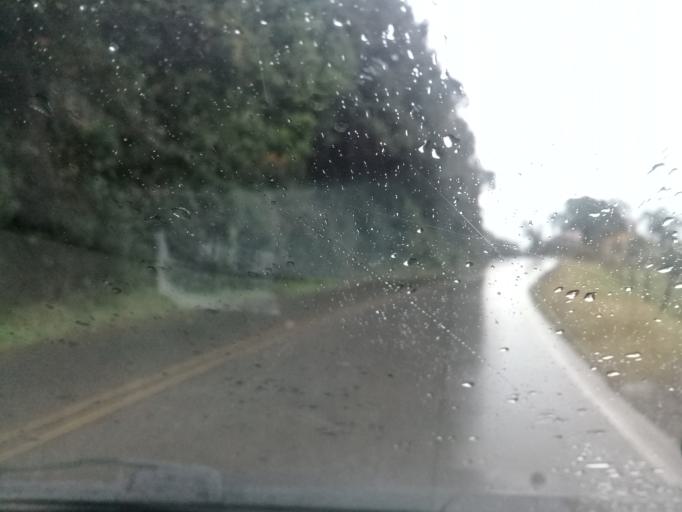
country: CO
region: Cundinamarca
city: Guasca
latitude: 4.8461
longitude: -73.8236
